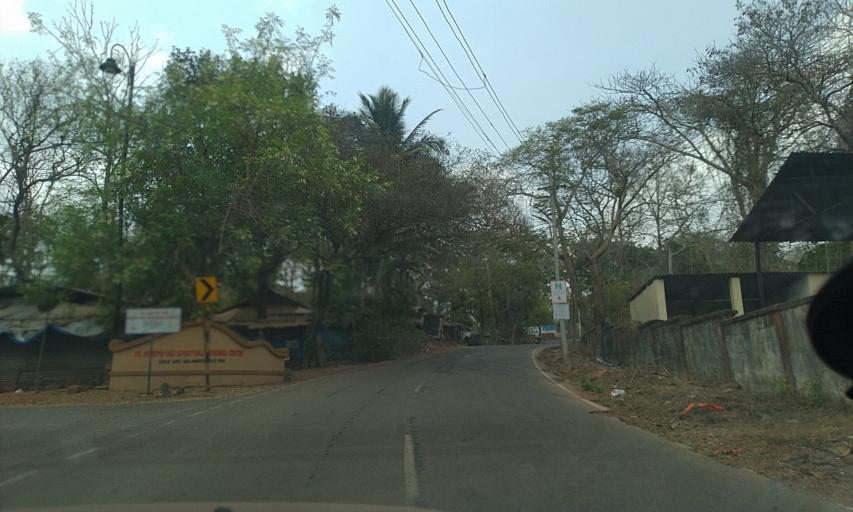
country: IN
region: Goa
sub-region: North Goa
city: Jua
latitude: 15.4945
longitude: 73.9115
